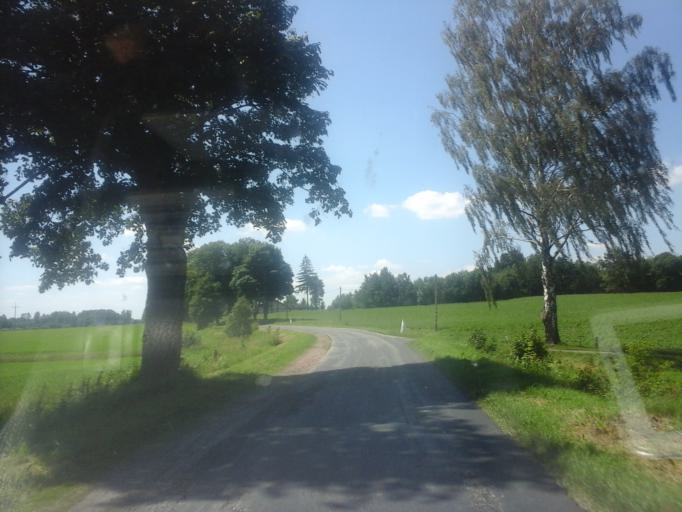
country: PL
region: West Pomeranian Voivodeship
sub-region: Powiat bialogardzki
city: Bialogard
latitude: 54.0707
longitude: 16.0387
